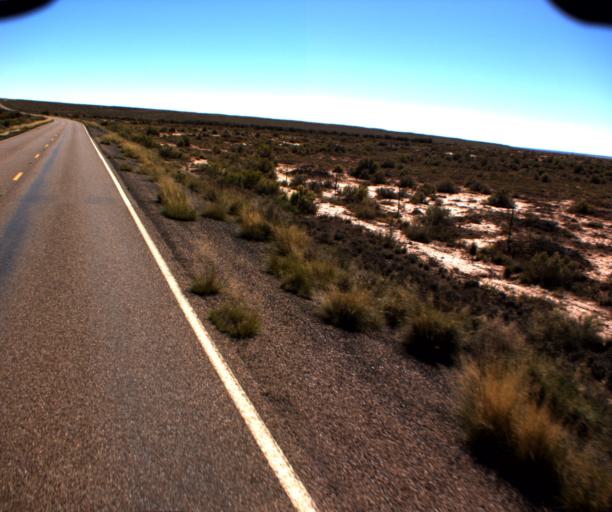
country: US
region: Arizona
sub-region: Navajo County
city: Holbrook
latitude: 35.0558
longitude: -110.0961
